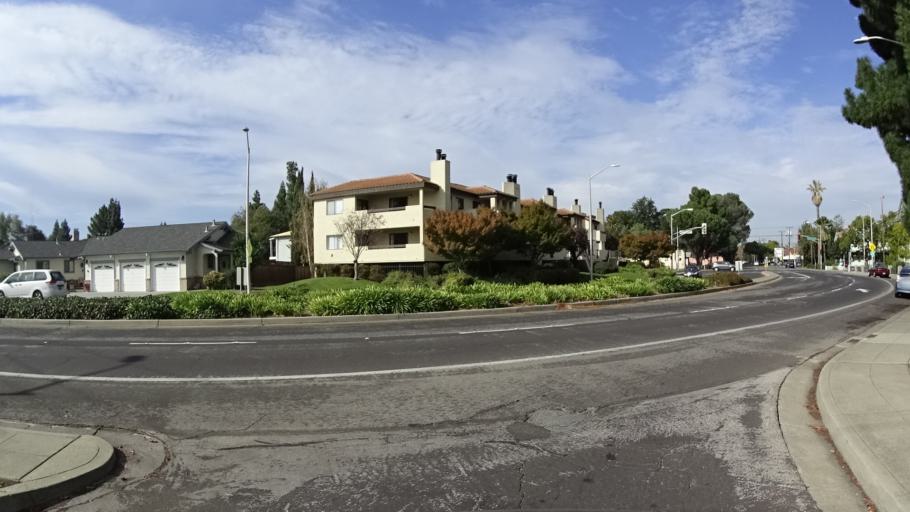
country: US
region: California
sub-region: Santa Clara County
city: Santa Clara
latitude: 37.3455
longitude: -121.9508
